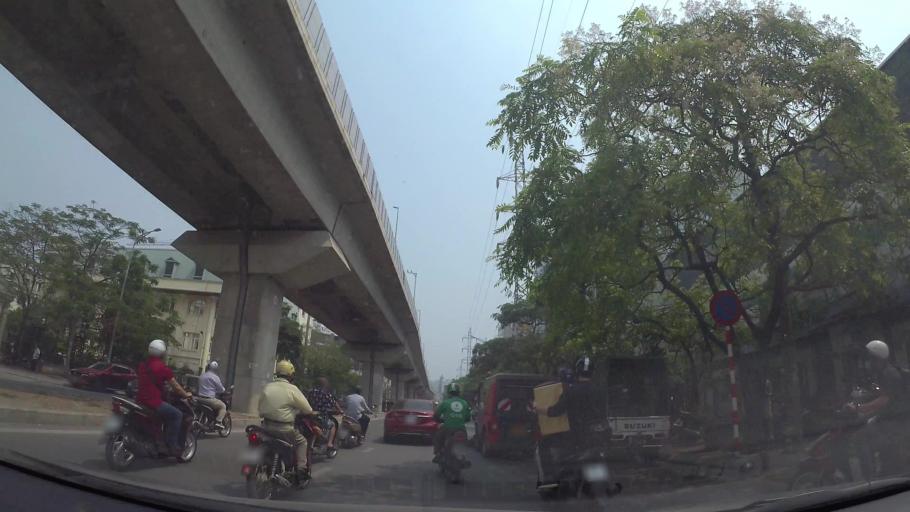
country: VN
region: Ha Noi
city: Dong Da
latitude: 21.0227
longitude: 105.8266
